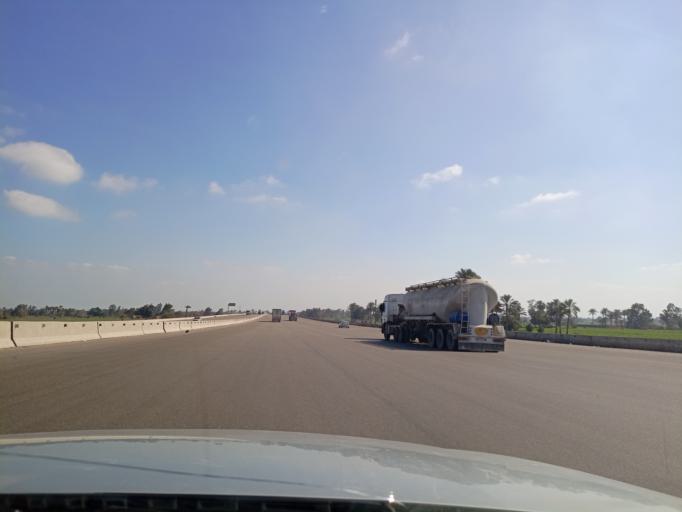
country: EG
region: Muhafazat al Qalyubiyah
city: Banha
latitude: 30.4657
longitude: 31.3014
